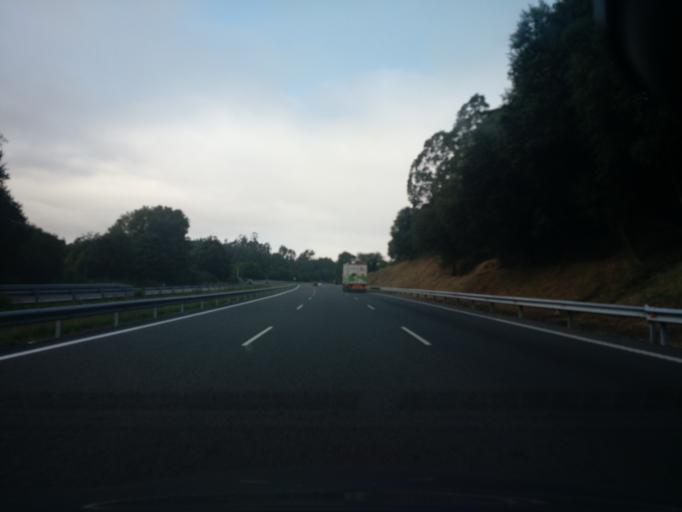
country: ES
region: Galicia
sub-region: Provincia da Coruna
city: Abegondo
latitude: 43.1842
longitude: -8.3113
